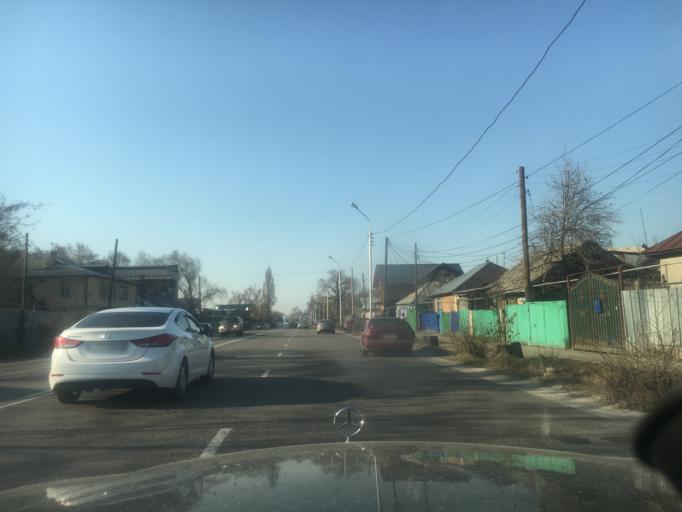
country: KZ
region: Almaty Qalasy
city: Almaty
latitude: 43.2814
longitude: 76.9396
